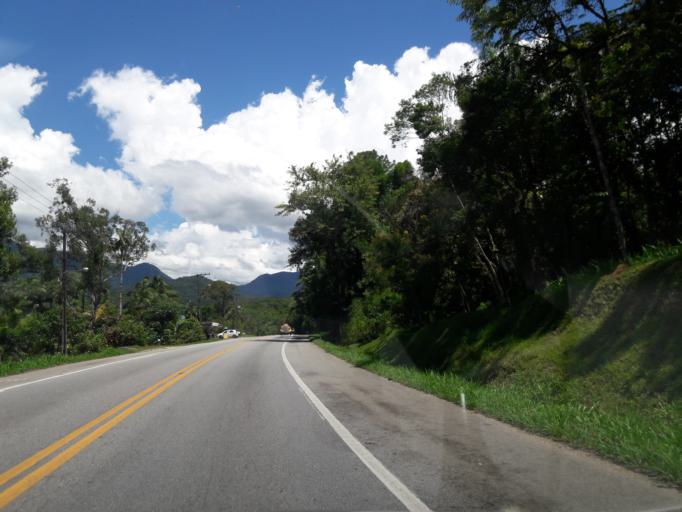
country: BR
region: Parana
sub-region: Antonina
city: Antonina
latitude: -25.5367
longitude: -48.7938
